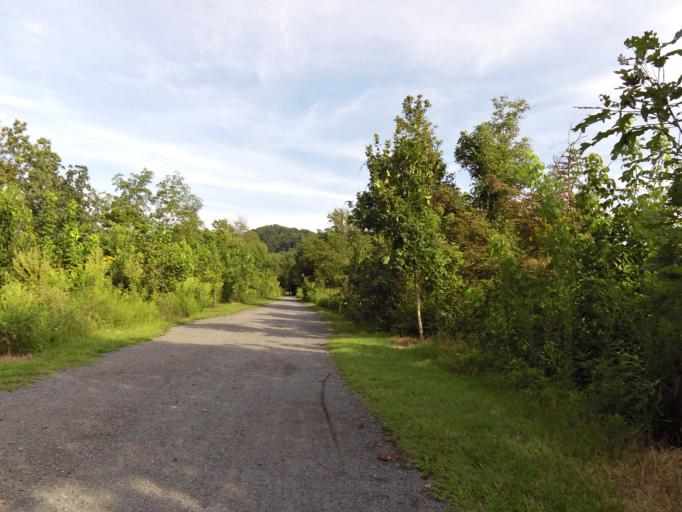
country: US
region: Virginia
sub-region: Washington County
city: Abingdon
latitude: 36.6993
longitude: -81.9537
